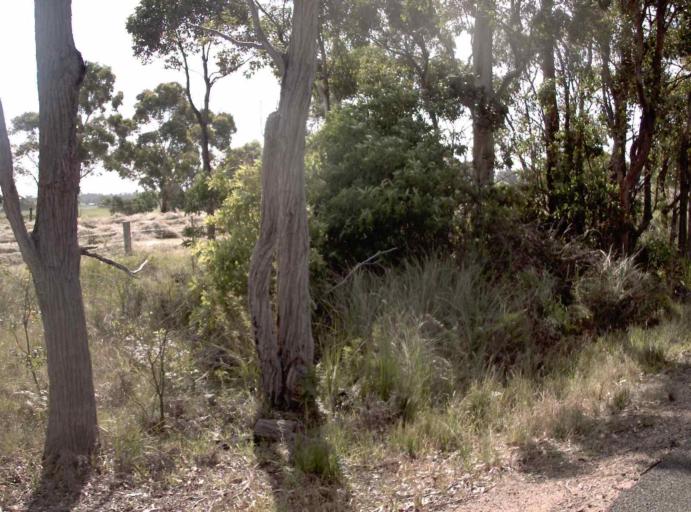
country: AU
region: Victoria
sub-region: East Gippsland
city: Lakes Entrance
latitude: -37.8430
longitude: 148.0380
